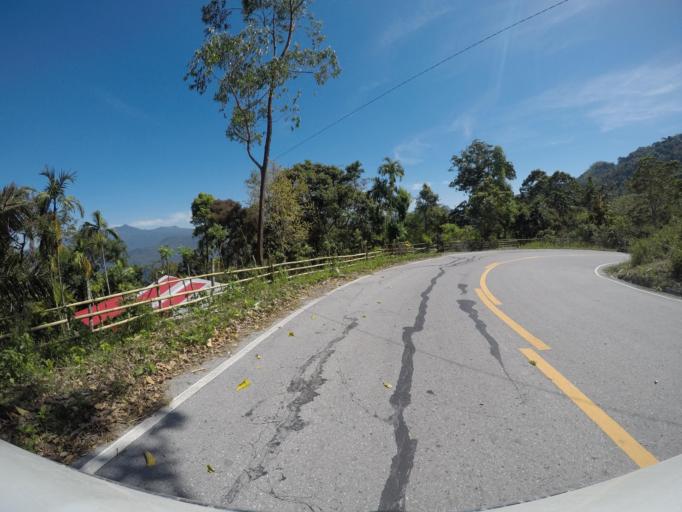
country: TL
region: Manufahi
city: Same
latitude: -8.9086
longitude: 125.9742
